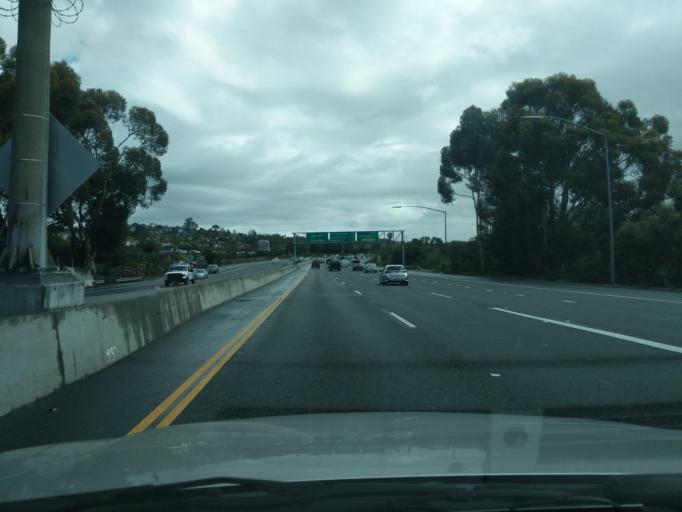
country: US
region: California
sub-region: San Diego County
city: Carlsbad
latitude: 33.1788
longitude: -117.3483
